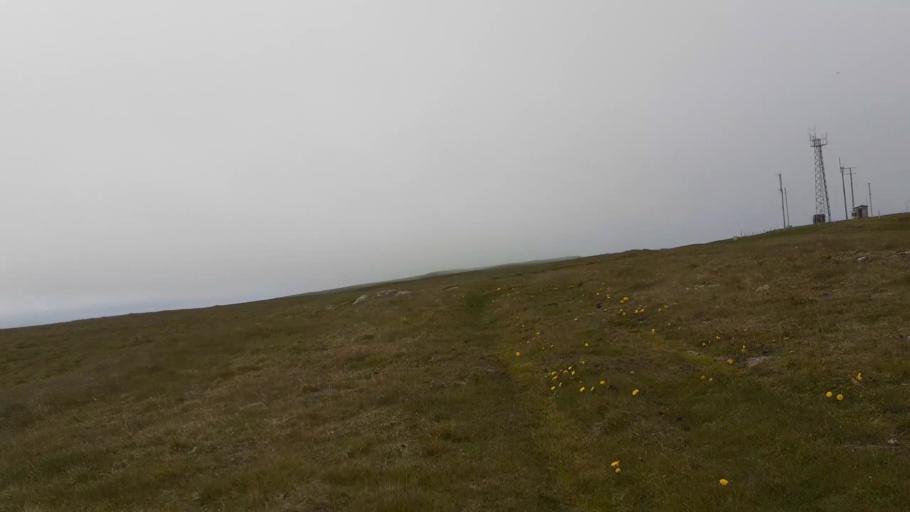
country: IS
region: Northeast
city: Dalvik
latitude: 66.5441
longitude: -17.9927
